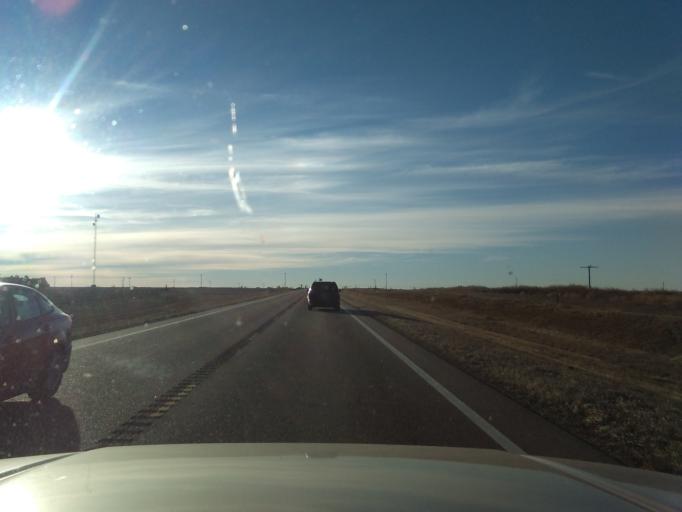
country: US
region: Kansas
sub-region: Thomas County
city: Colby
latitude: 39.4559
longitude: -100.7900
